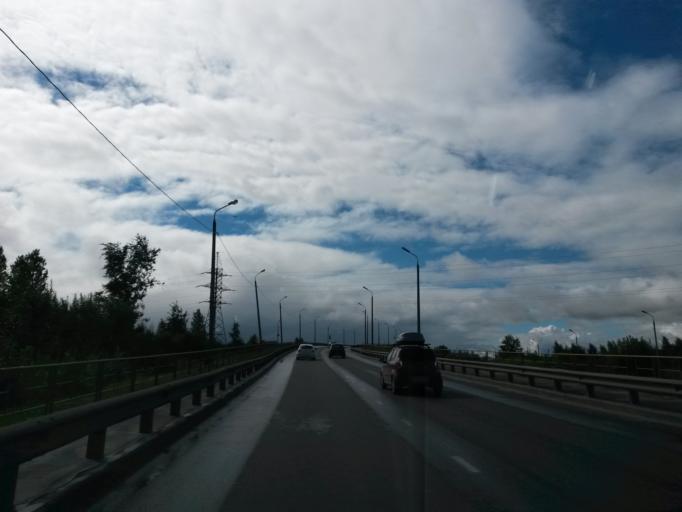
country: RU
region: Jaroslavl
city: Yaroslavl
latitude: 57.6704
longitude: 39.7690
